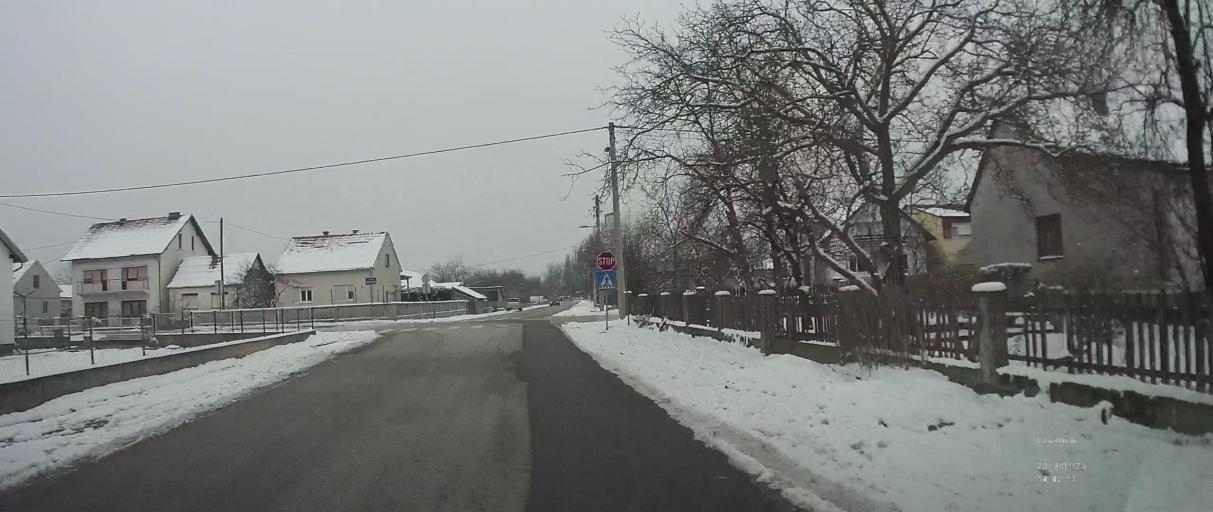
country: HR
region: Zagrebacka
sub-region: Grad Velika Gorica
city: Velika Gorica
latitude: 45.7046
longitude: 16.0747
